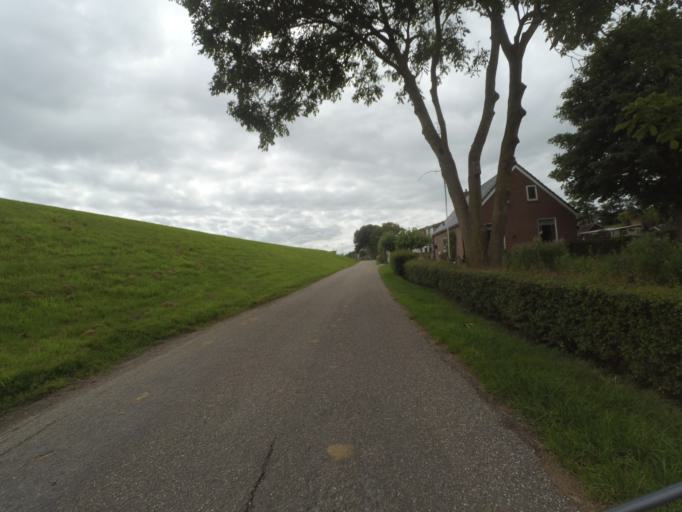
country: NL
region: Friesland
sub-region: Gemeente Dongeradeel
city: Anjum
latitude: 53.3600
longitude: 6.1499
